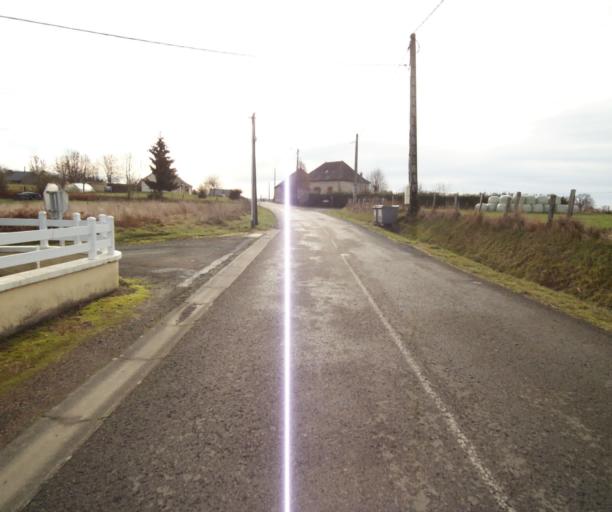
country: FR
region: Limousin
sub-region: Departement de la Correze
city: Chameyrat
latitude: 45.2411
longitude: 1.6996
